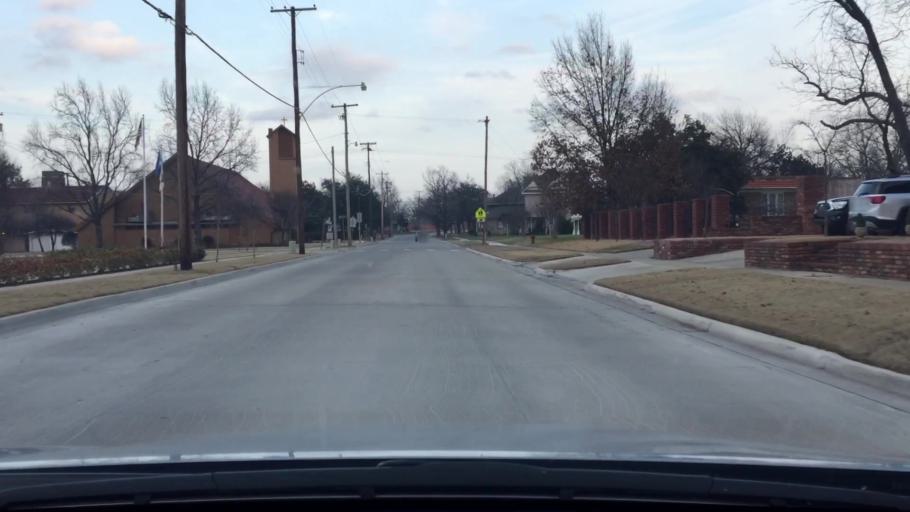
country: US
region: Oklahoma
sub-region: Carter County
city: Ardmore
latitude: 34.1710
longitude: -97.1367
